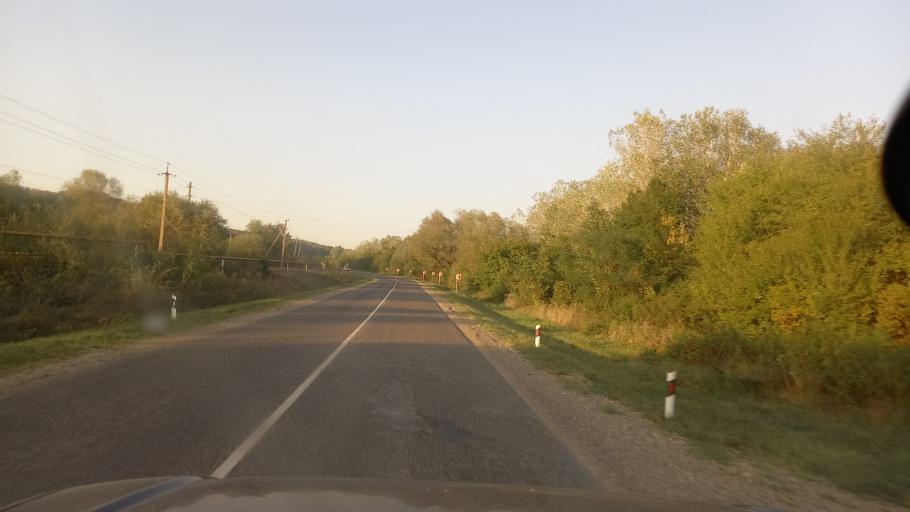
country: RU
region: Krasnodarskiy
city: Smolenskaya
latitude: 44.7565
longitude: 38.7664
